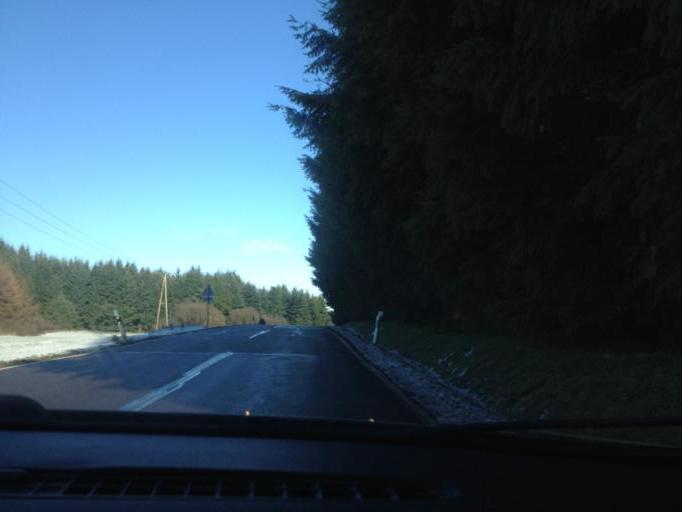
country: DE
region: Saarland
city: Freisen
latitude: 49.5360
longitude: 7.2258
